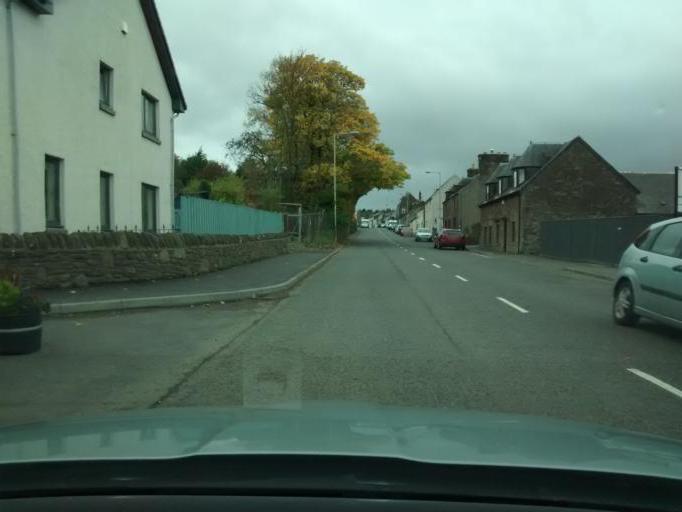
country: GB
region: Scotland
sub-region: Perth and Kinross
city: Auchterarder
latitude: 56.3001
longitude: -3.6940
